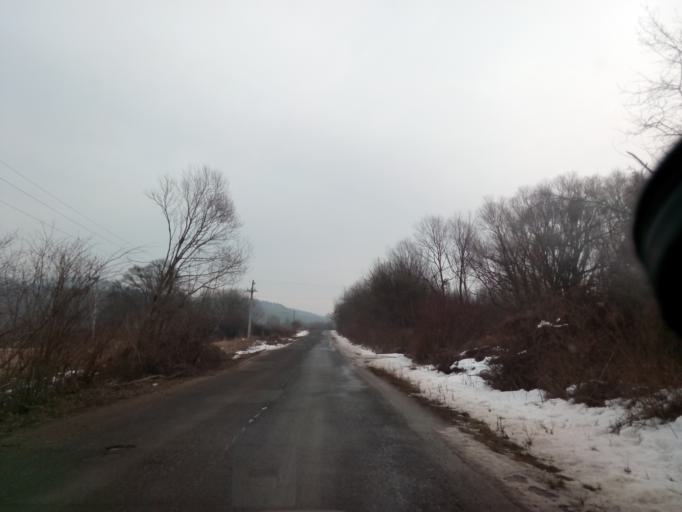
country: HU
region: Borsod-Abauj-Zemplen
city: Gonc
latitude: 48.5060
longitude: 21.3245
